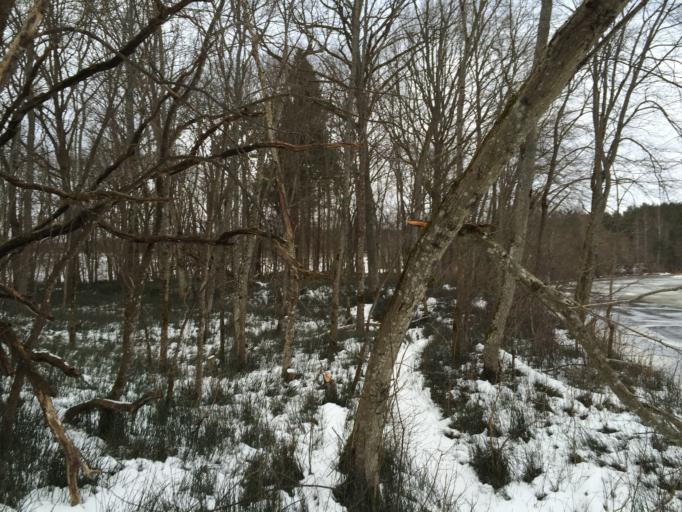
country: LV
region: Seja
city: Loja
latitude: 57.1267
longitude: 24.6613
